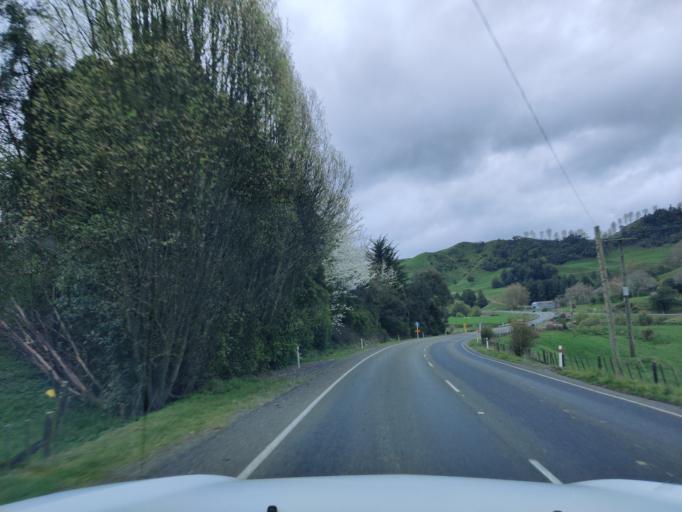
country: NZ
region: Waikato
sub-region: Otorohanga District
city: Otorohanga
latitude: -38.4906
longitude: 175.1875
